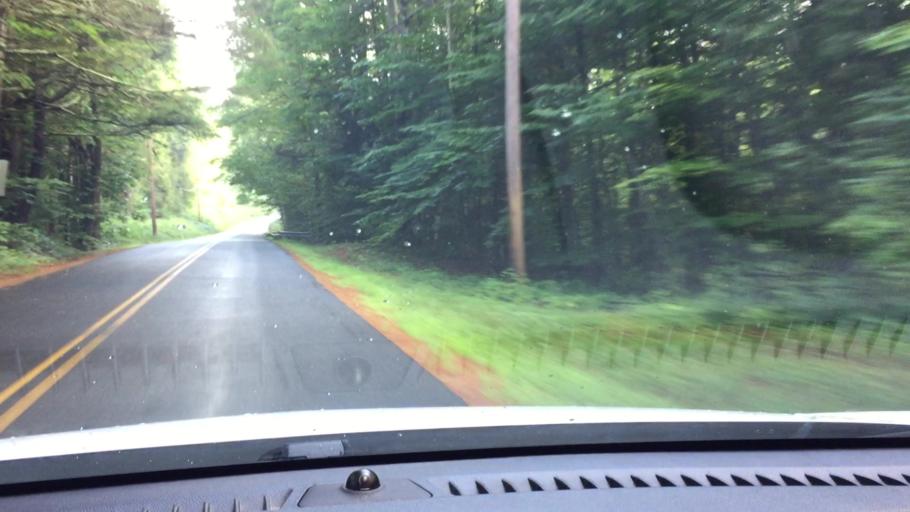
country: US
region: Massachusetts
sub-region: Berkshire County
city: Becket
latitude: 42.4039
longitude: -72.9791
